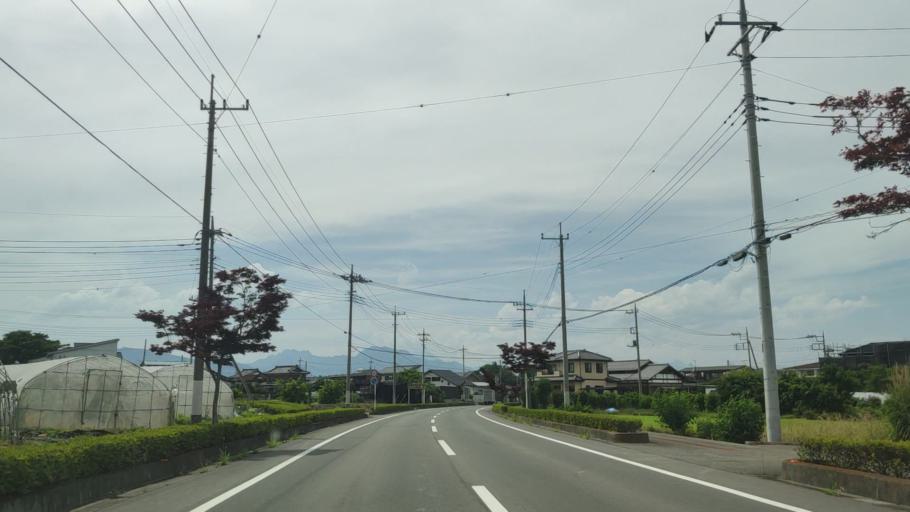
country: JP
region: Gunma
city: Tomioka
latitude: 36.2484
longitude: 138.8845
